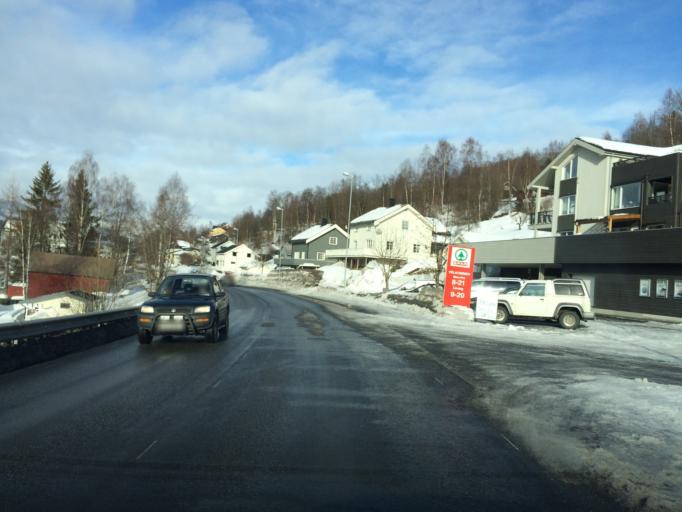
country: NO
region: Oppland
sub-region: Gausdal
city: Segalstad bru
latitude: 61.2264
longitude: 10.2271
